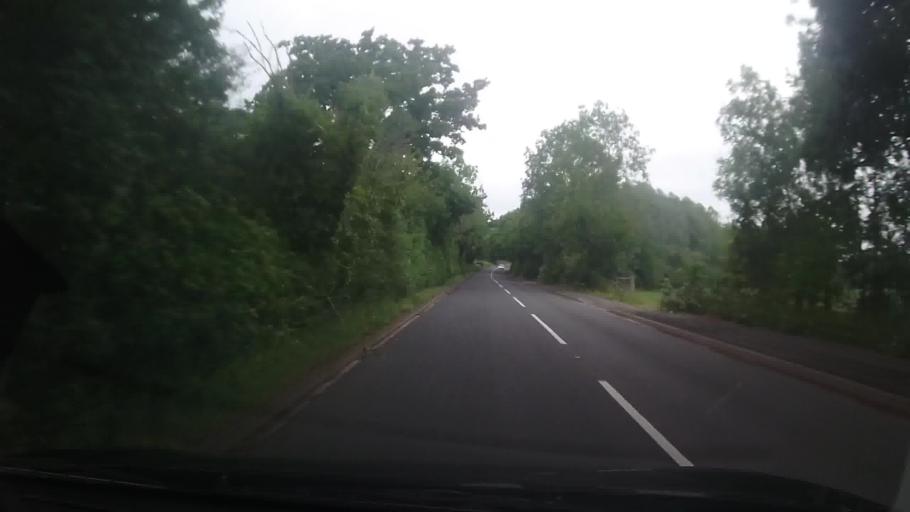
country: GB
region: England
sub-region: Shropshire
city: Shrewsbury
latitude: 52.7215
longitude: -2.7652
